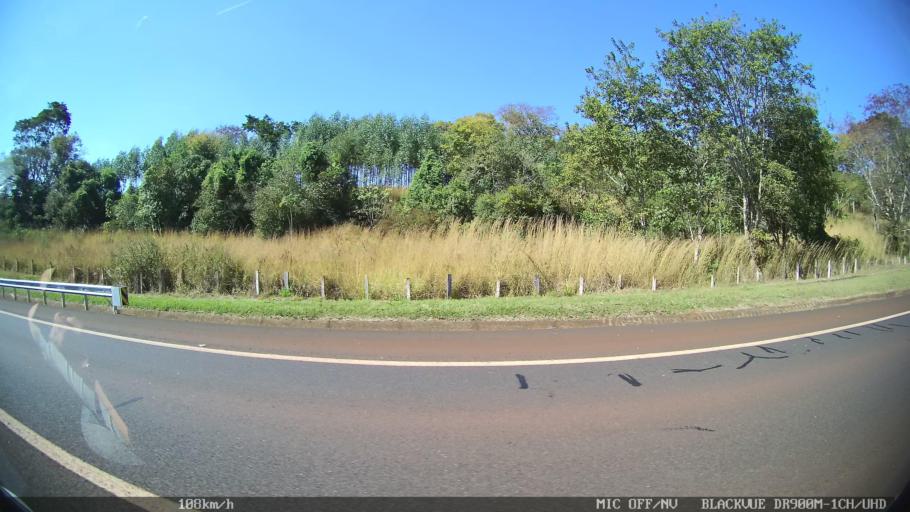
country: BR
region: Sao Paulo
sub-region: Franca
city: Franca
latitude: -20.6200
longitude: -47.4589
